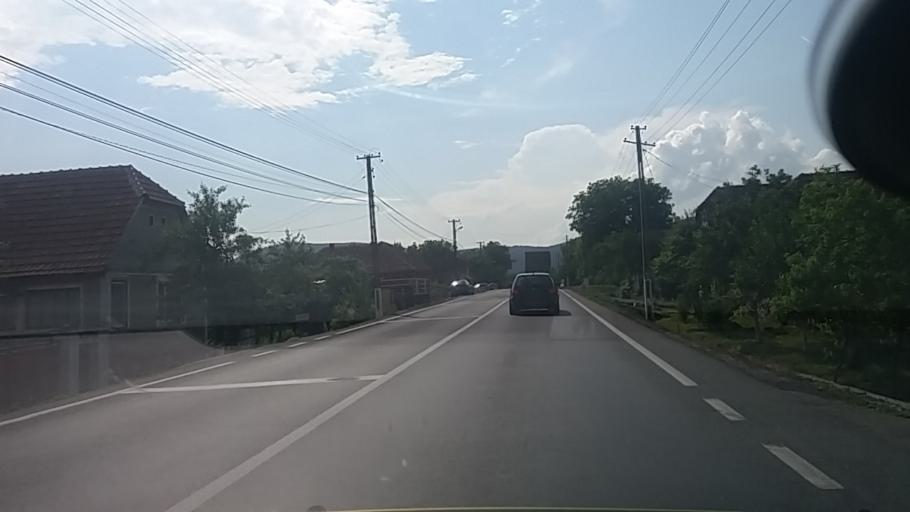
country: RO
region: Arad
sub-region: Comuna Barzava
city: Barzava
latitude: 46.1105
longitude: 21.9763
